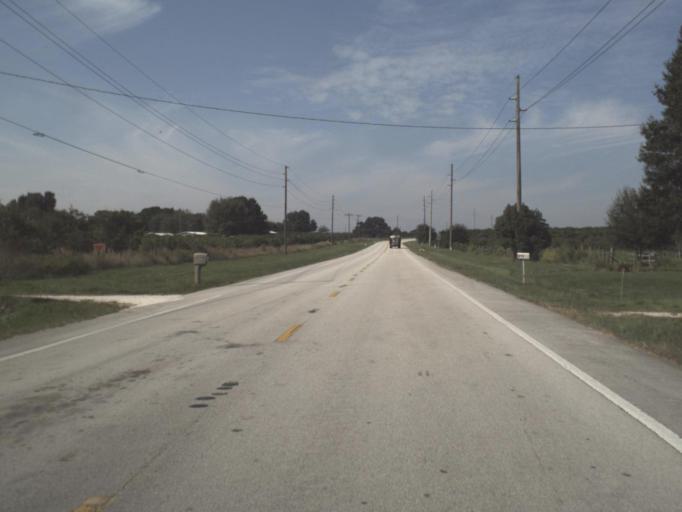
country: US
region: Florida
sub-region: Hardee County
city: Wauchula
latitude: 27.5605
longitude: -81.6660
